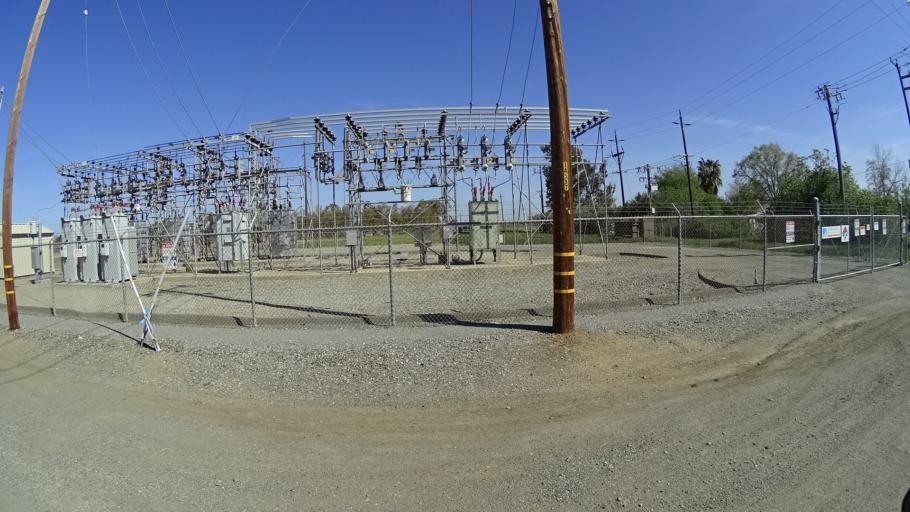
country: US
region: California
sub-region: Glenn County
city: Willows
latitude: 39.5314
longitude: -122.1861
